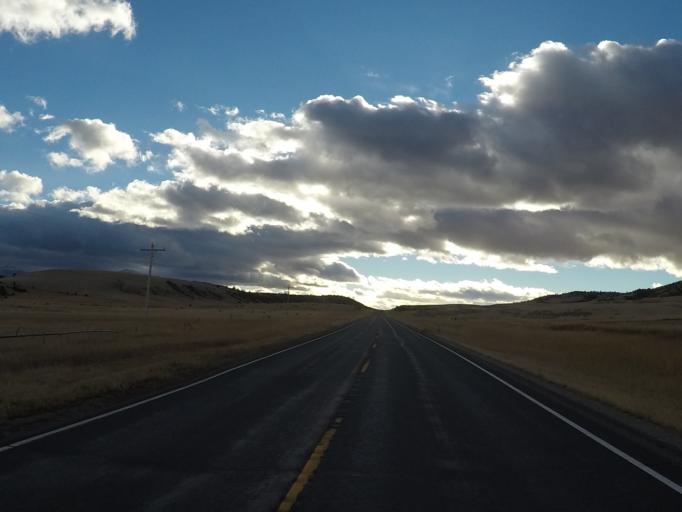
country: US
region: Montana
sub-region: Jefferson County
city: Whitehall
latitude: 45.9153
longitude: -111.9339
